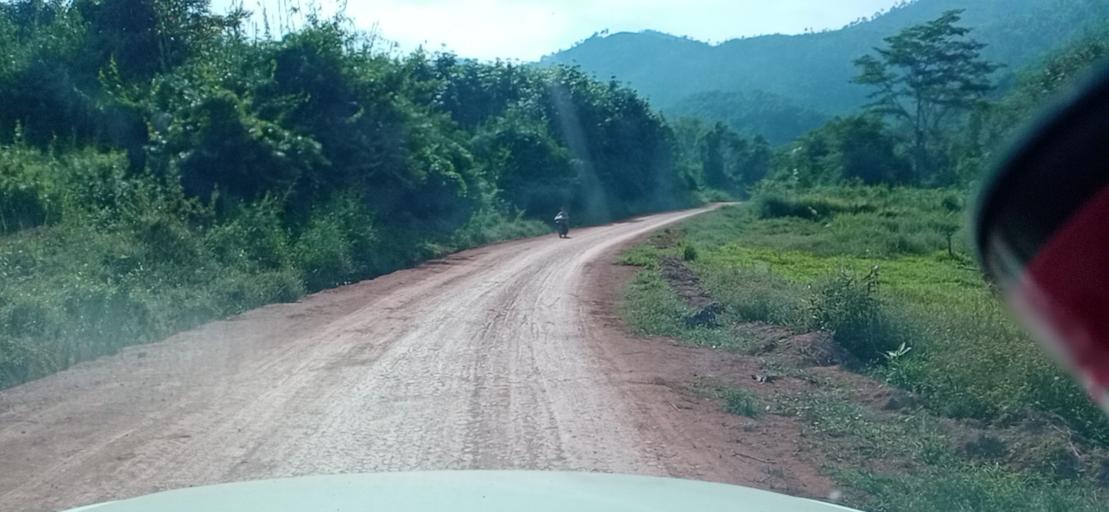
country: TH
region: Changwat Bueng Kan
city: Pak Khat
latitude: 18.6696
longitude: 103.2007
